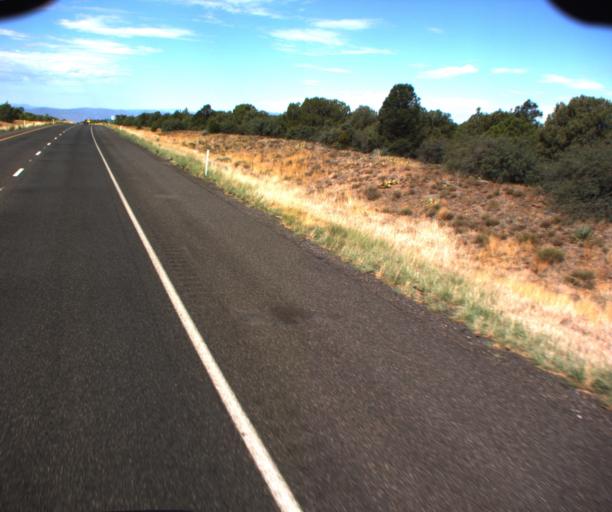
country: US
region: Arizona
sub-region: Yavapai County
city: Village of Oak Creek (Big Park)
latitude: 34.7590
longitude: -111.6640
